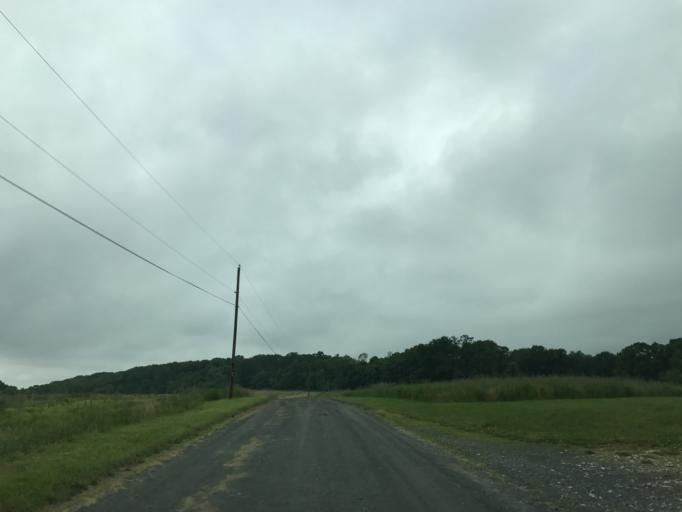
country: US
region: Maryland
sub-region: Harford County
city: Jarrettsville
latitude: 39.6834
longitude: -76.4676
